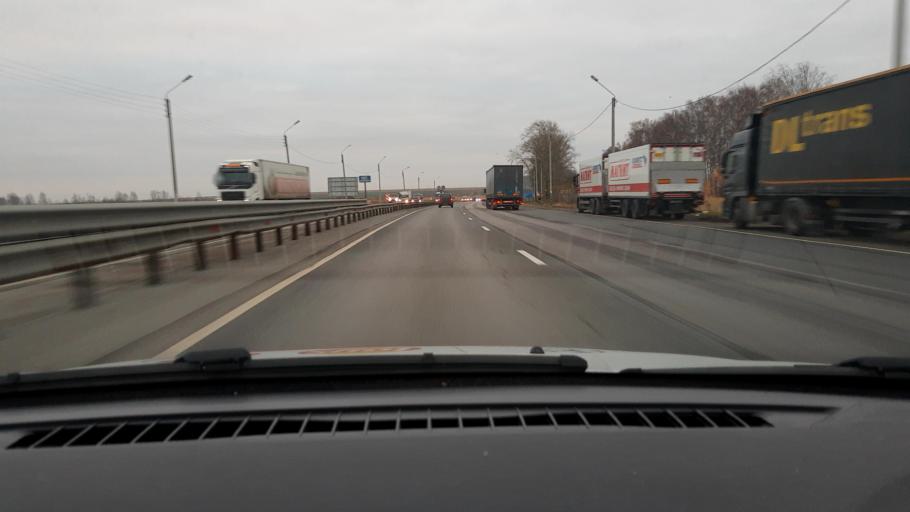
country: RU
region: Nizjnij Novgorod
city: Kstovo
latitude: 56.1248
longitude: 44.2667
